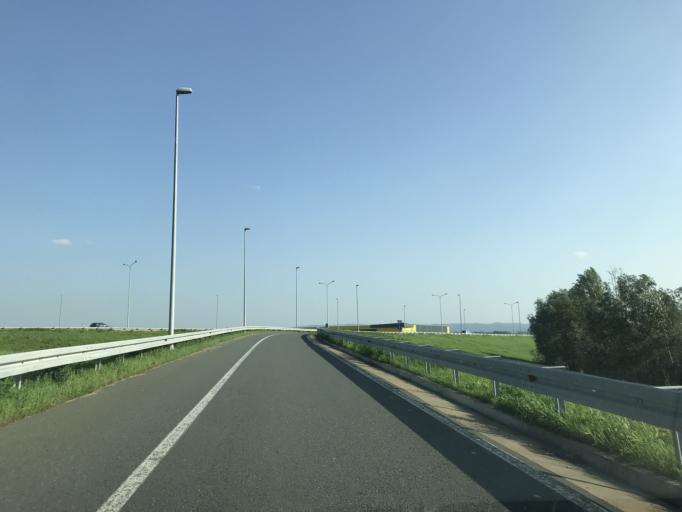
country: RS
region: Autonomna Pokrajina Vojvodina
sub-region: Juznobacki Okrug
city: Novi Sad
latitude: 45.3032
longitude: 19.8594
